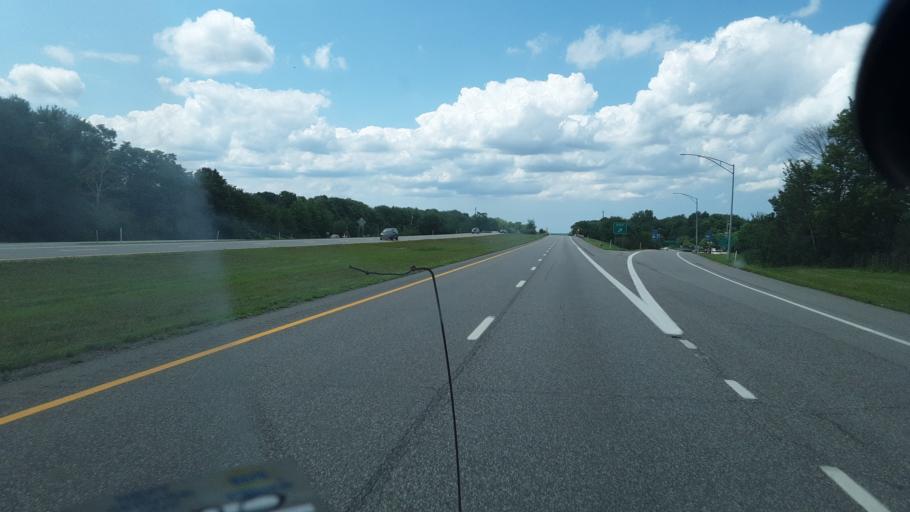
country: US
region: Ohio
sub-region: Geauga County
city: Bainbridge
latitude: 41.3876
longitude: -81.3347
